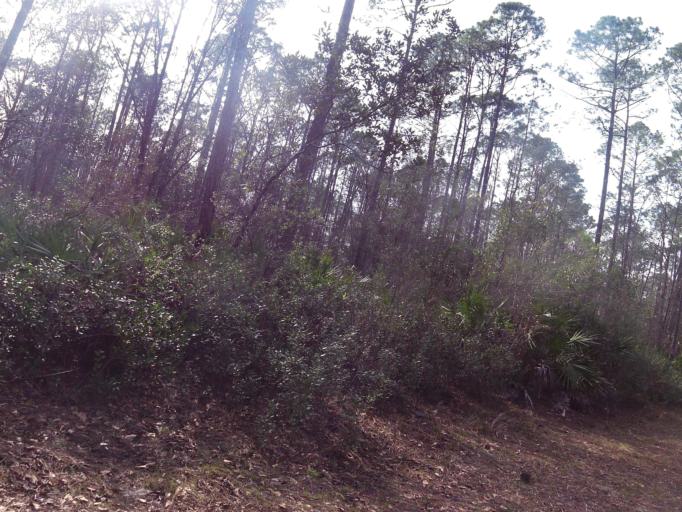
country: US
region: Florida
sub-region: Clay County
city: Middleburg
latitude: 30.1139
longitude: -81.9006
